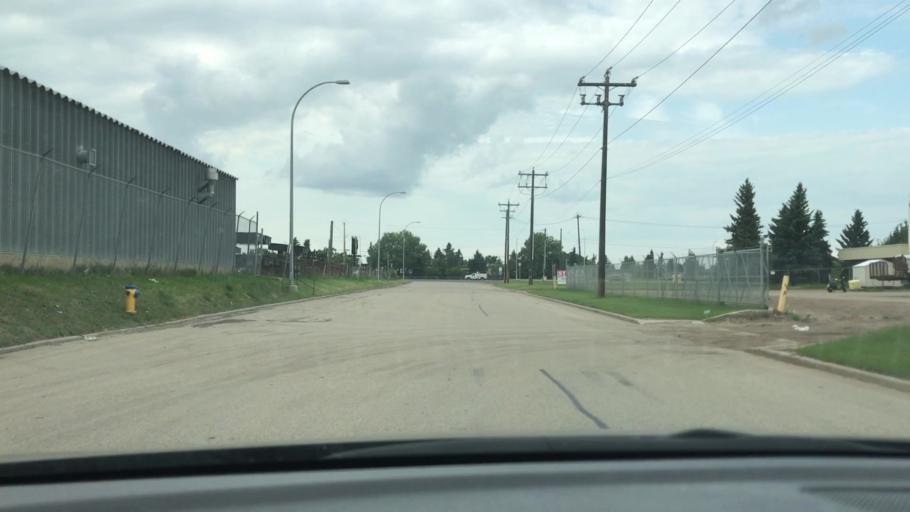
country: CA
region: Alberta
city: Edmonton
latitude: 53.5394
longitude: -113.4150
